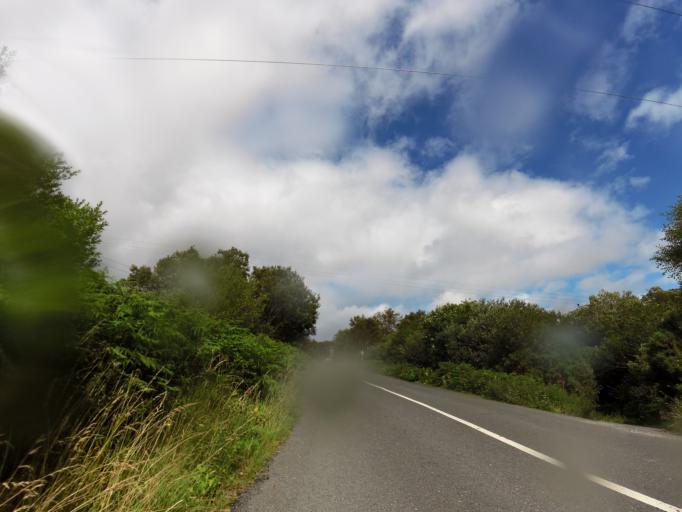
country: IE
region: Connaught
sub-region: County Galway
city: Oughterard
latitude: 53.4158
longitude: -9.3311
